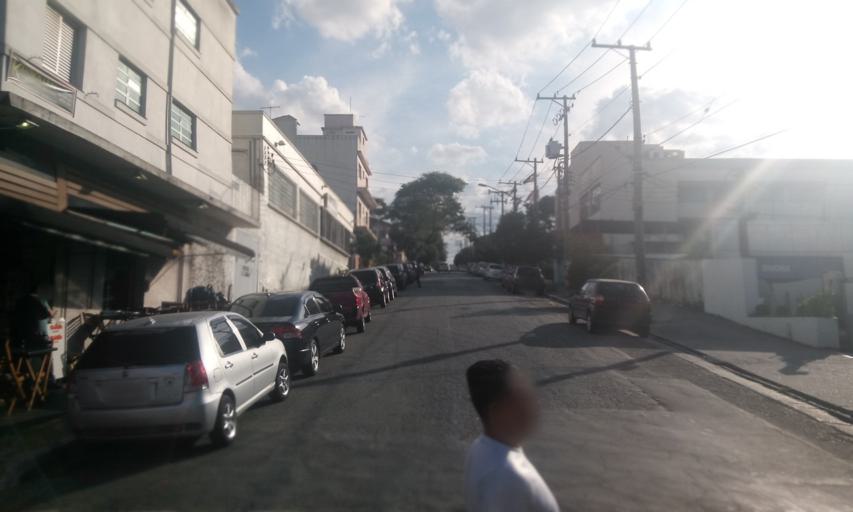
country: BR
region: Sao Paulo
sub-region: Sao Paulo
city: Sao Paulo
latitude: -23.5980
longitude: -46.6098
